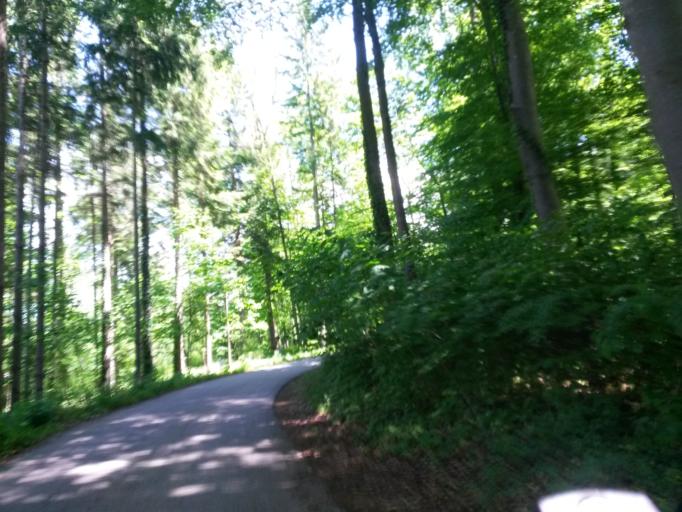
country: DE
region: Baden-Wuerttemberg
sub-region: Tuebingen Region
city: Aulendorf
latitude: 47.9680
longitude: 9.6658
